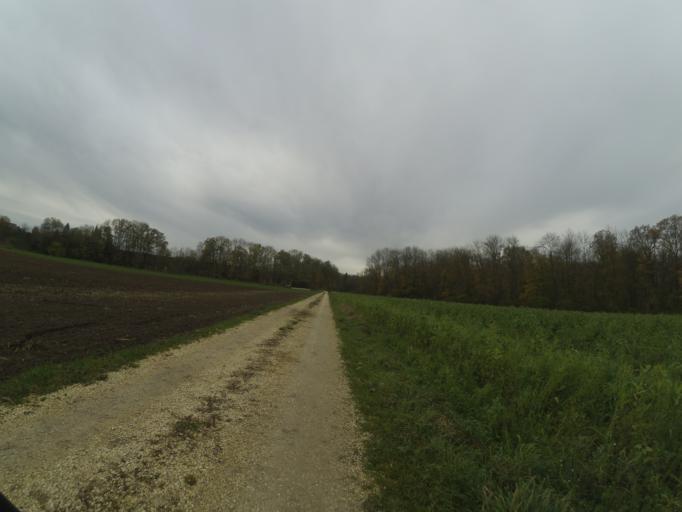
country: DE
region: Bavaria
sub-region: Swabia
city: Senden
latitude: 48.3424
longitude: 10.0053
